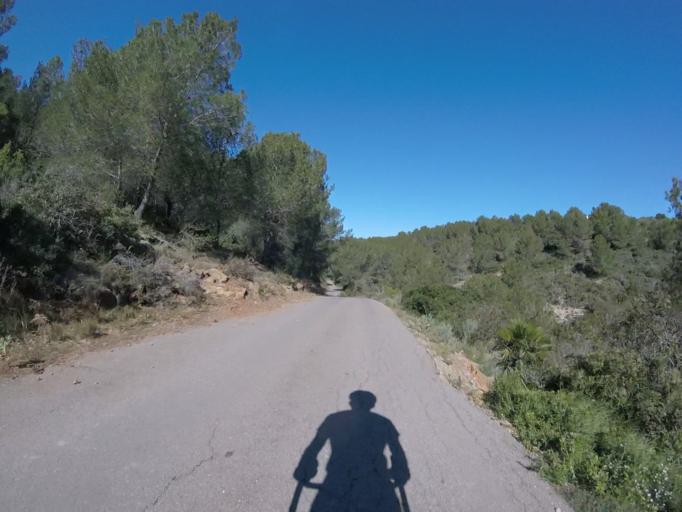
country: ES
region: Valencia
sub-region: Provincia de Castello
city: Benicassim
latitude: 40.0805
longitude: 0.0891
